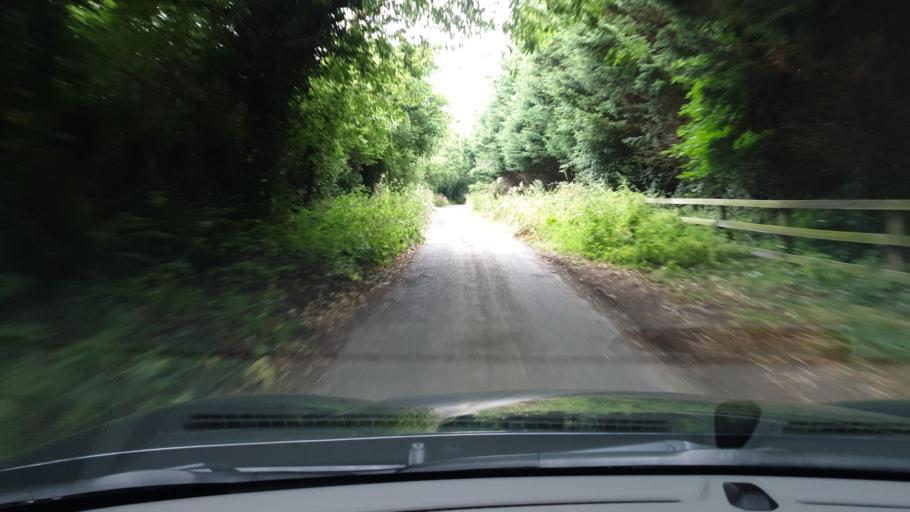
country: IE
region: Leinster
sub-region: An Mhi
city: Ashbourne
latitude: 53.5372
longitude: -6.3890
